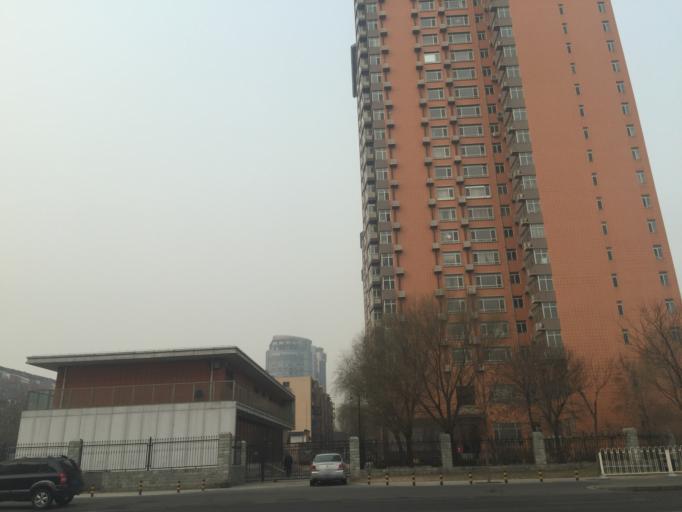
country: CN
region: Beijing
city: Datun
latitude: 40.0000
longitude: 116.3806
